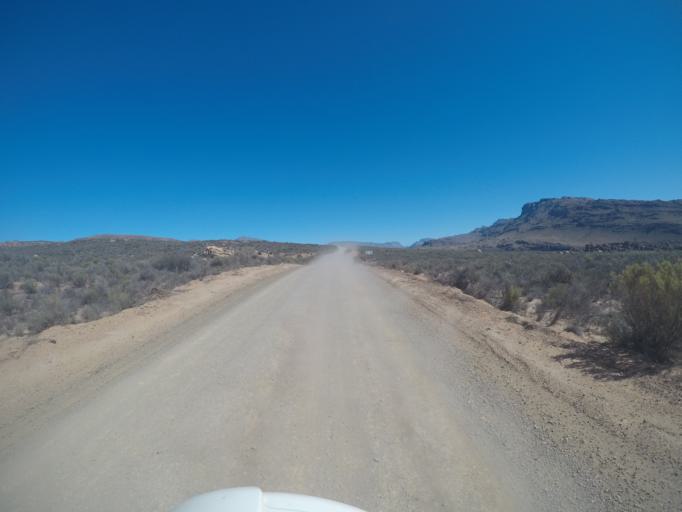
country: ZA
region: Western Cape
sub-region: West Coast District Municipality
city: Clanwilliam
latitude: -32.5070
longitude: 19.3046
